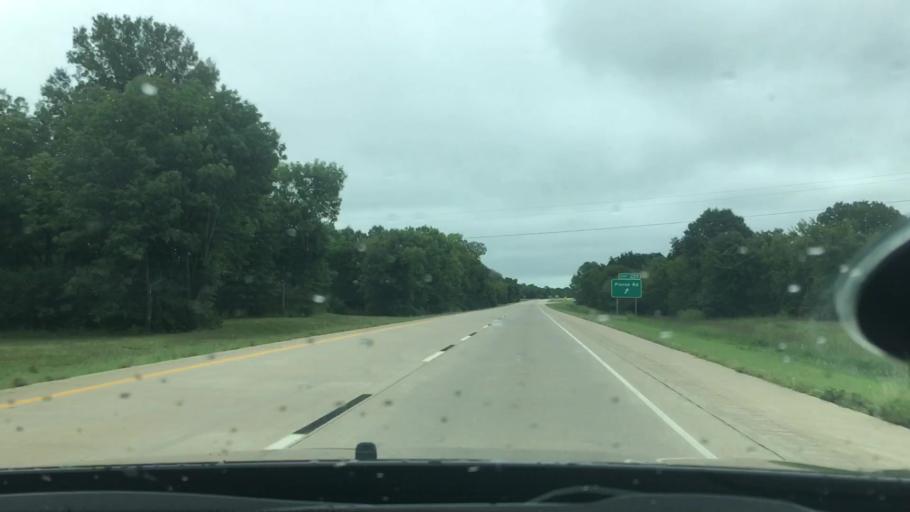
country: US
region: Oklahoma
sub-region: McIntosh County
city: Checotah
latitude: 35.4508
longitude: -95.7251
